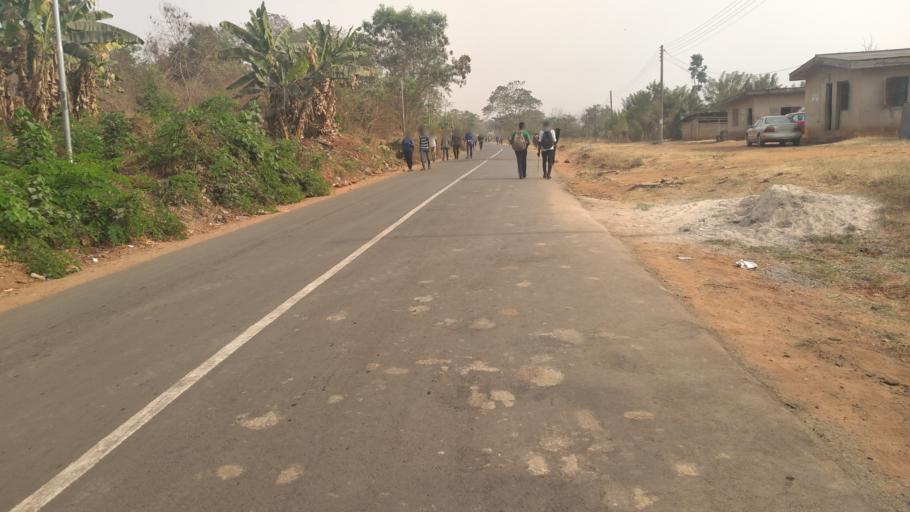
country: NG
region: Ondo
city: Ilare
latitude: 7.3007
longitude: 5.1447
